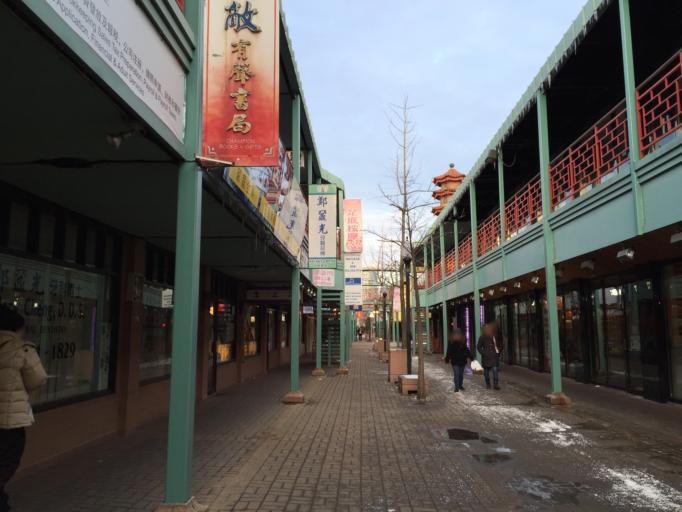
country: US
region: Illinois
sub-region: Cook County
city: Chicago
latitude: 41.8535
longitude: -87.6350
